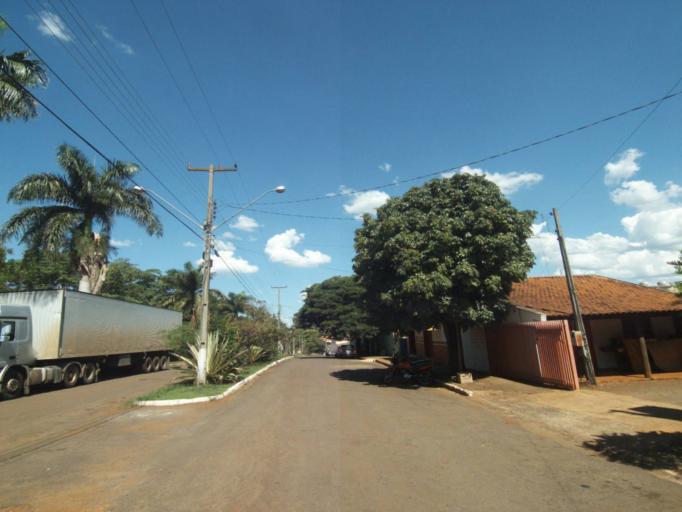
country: BR
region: Parana
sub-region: Sertanopolis
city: Sertanopolis
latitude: -23.0335
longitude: -50.8201
